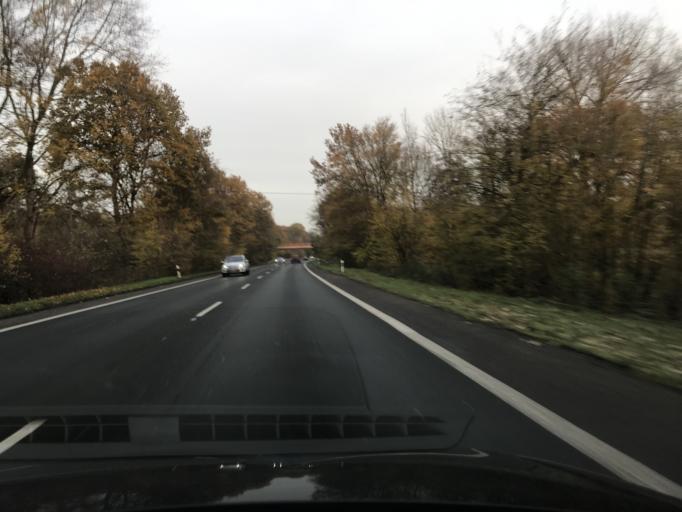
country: DE
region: North Rhine-Westphalia
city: Werne
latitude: 51.6999
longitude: 7.6791
